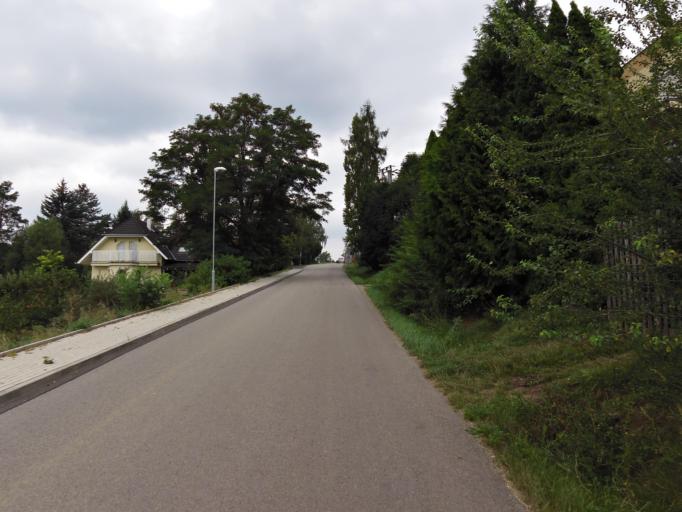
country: CZ
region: Central Bohemia
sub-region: Okres Benesov
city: Cercany
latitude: 49.8699
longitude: 14.7107
